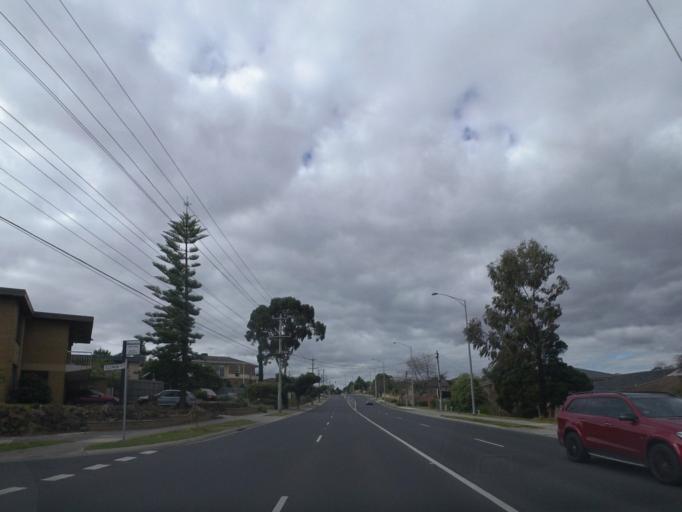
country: AU
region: Victoria
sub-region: Manningham
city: Doncaster
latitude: -37.7834
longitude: 145.1087
